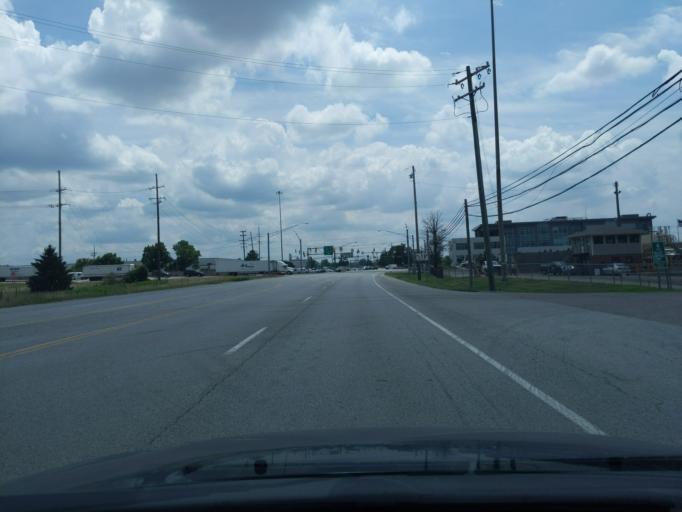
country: US
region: Ohio
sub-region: Hamilton County
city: Sharonville
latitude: 39.2865
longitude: -84.4293
